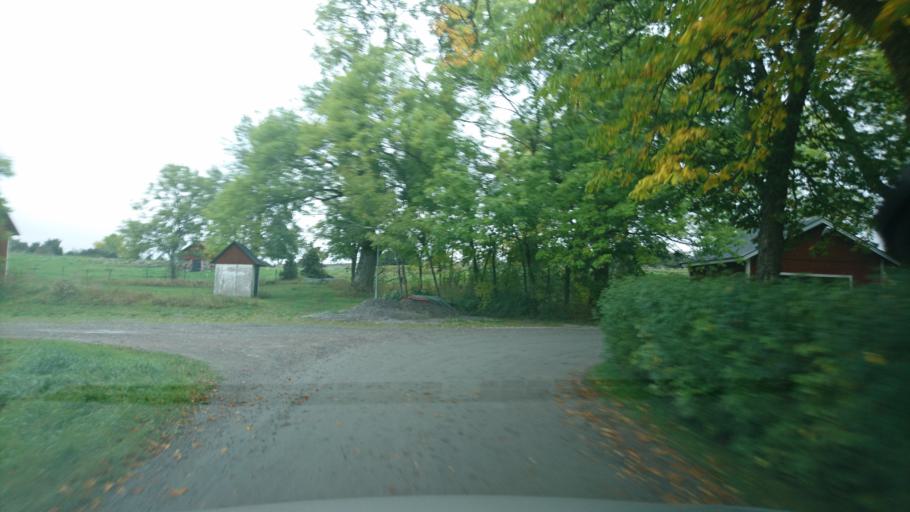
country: SE
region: Uppsala
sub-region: Uppsala Kommun
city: Saevja
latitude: 59.8639
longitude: 17.7236
